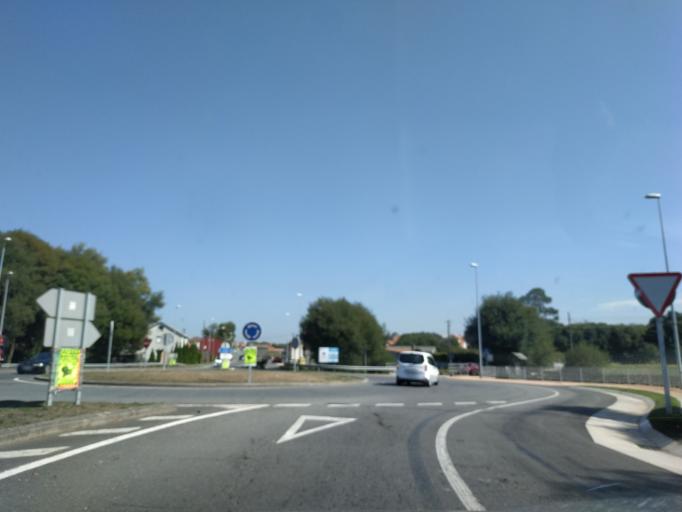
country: ES
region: Galicia
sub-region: Provincia da Coruna
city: Laracha
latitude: 43.2515
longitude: -8.6100
